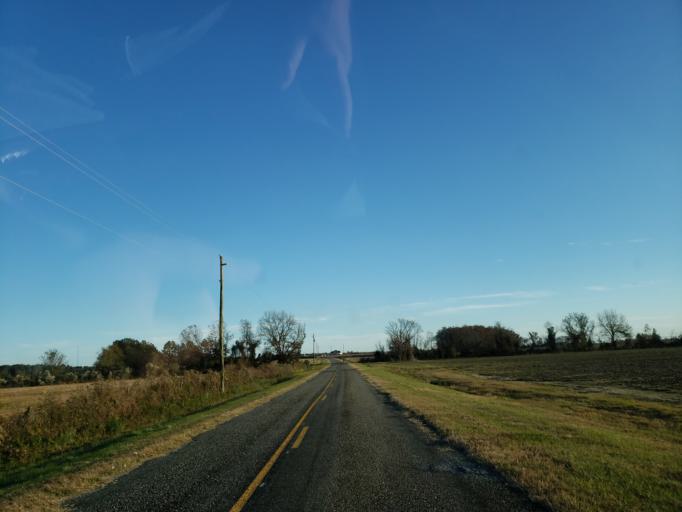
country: US
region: Georgia
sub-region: Dooly County
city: Unadilla
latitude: 32.1945
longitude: -83.7842
